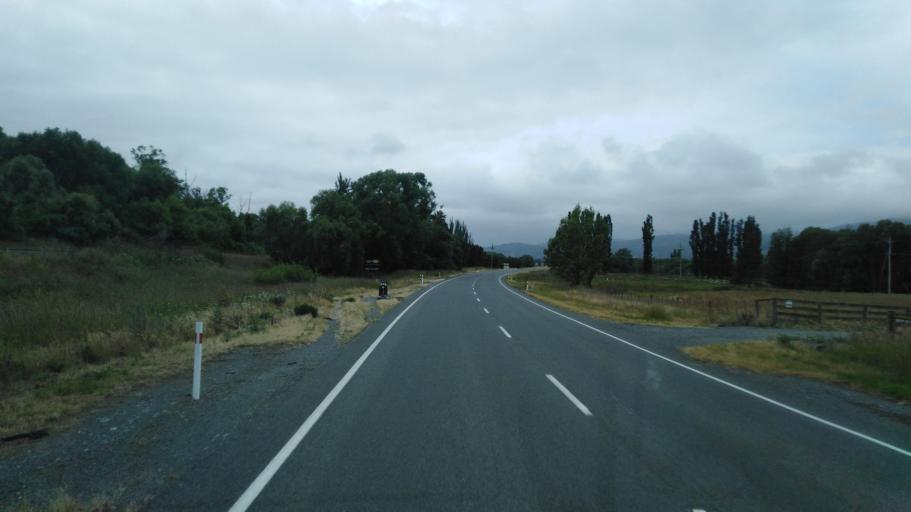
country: NZ
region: Canterbury
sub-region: Kaikoura District
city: Kaikoura
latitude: -42.7300
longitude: 173.2759
